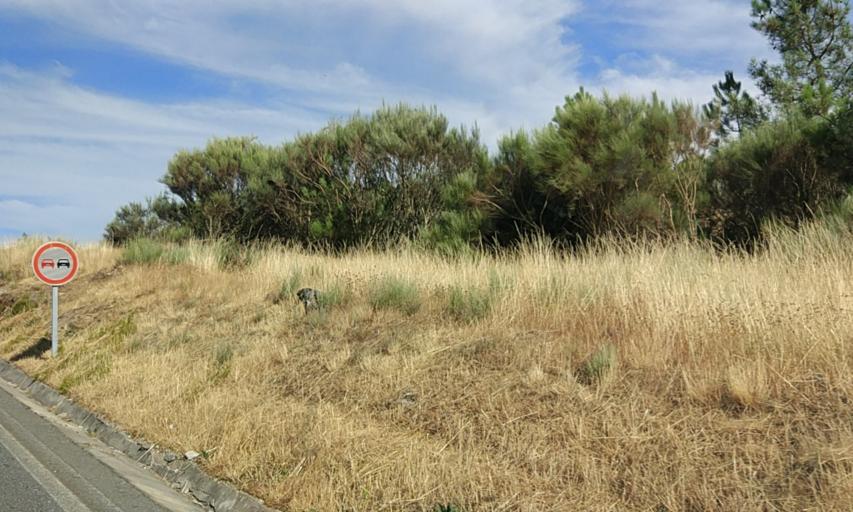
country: PT
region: Vila Real
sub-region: Murca
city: Murca
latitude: 41.3779
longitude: -7.5482
